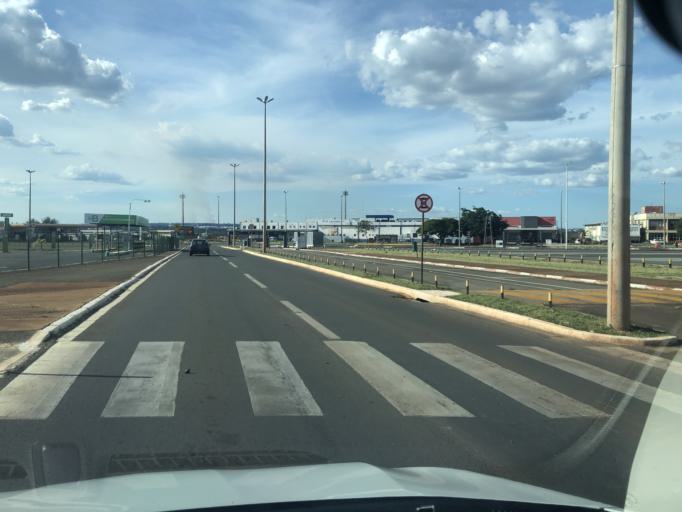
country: BR
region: Federal District
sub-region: Brasilia
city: Brasilia
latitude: -15.8694
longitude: -47.9236
